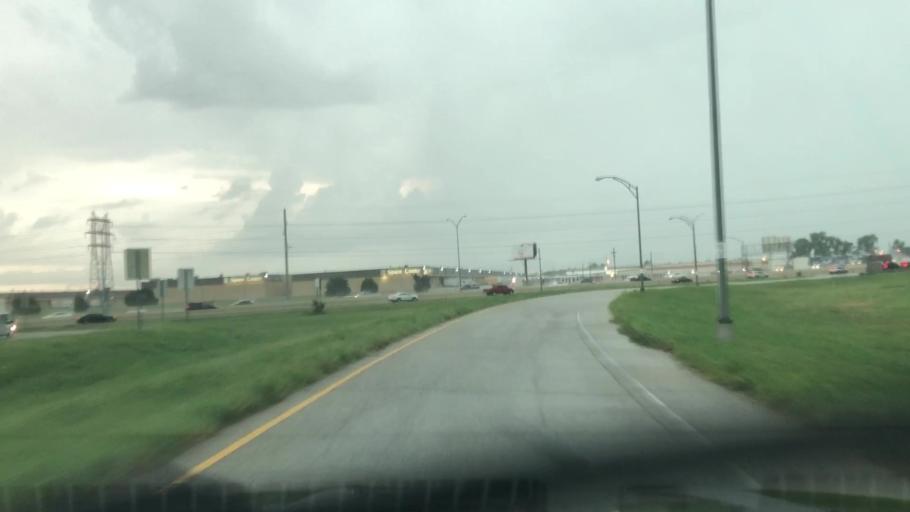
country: US
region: Oklahoma
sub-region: Tulsa County
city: Tulsa
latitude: 36.1140
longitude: -95.8990
